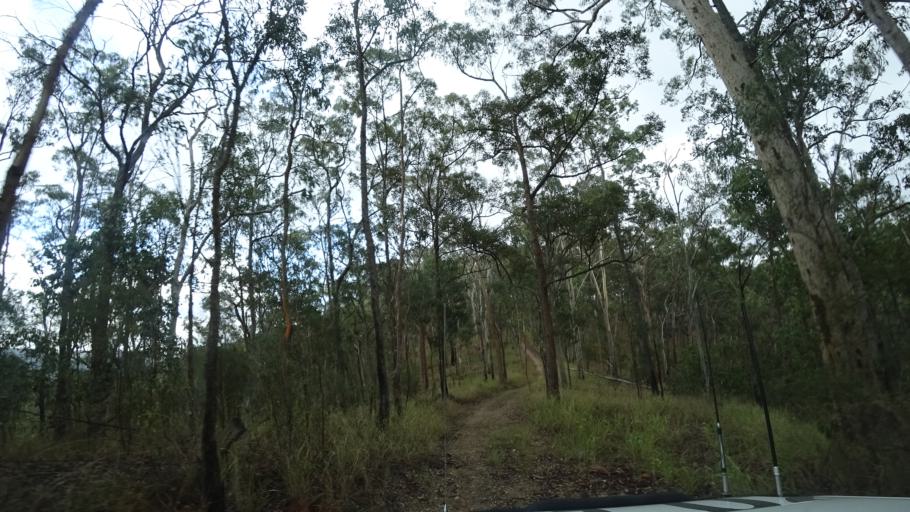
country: AU
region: Queensland
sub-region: Brisbane
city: Pullenvale
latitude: -27.4625
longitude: 152.8596
